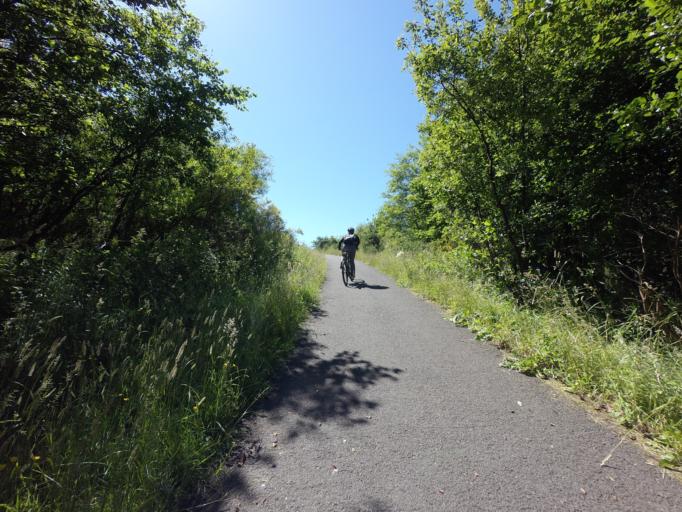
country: GB
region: Scotland
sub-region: West Lothian
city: West Calder
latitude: 55.8851
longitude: -3.5842
